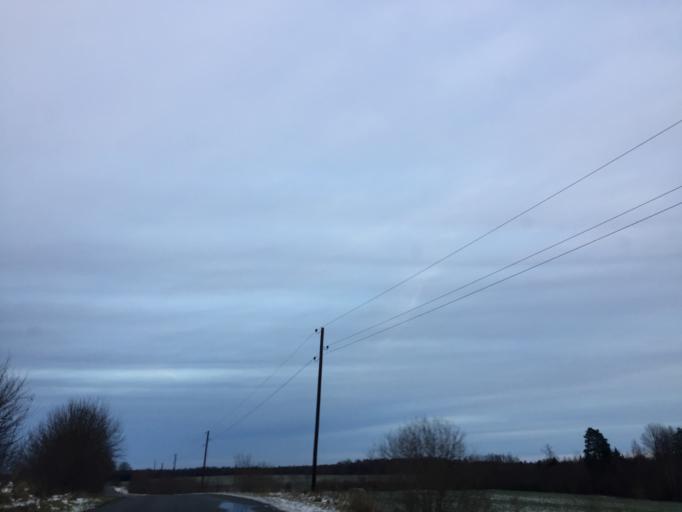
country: LV
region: Aloja
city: Aloja
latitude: 57.6162
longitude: 24.9213
